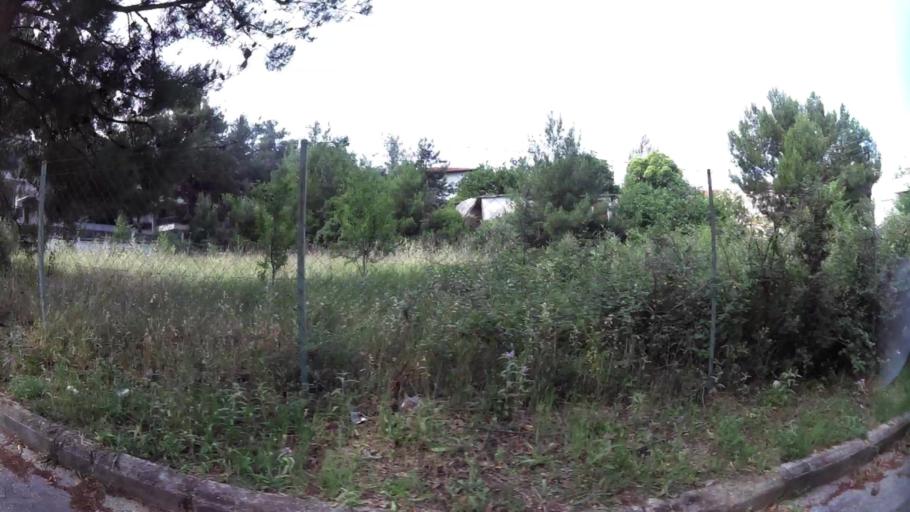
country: GR
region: Central Macedonia
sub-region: Nomos Thessalonikis
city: Panorama
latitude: 40.5807
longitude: 23.0274
